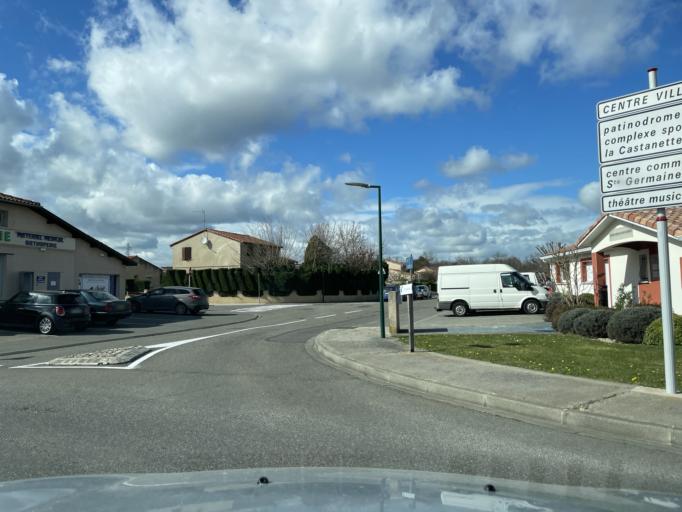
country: FR
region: Midi-Pyrenees
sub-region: Departement de la Haute-Garonne
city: Pibrac
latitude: 43.6158
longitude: 1.2778
